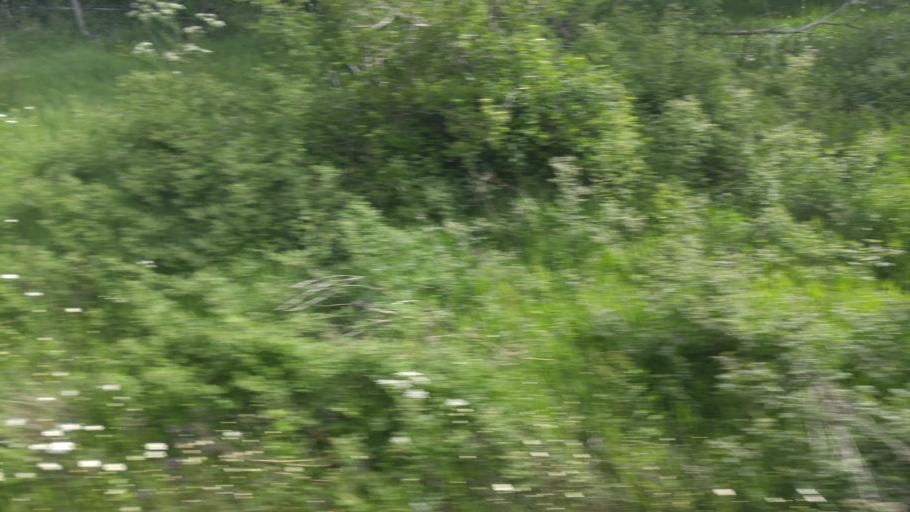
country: NO
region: Sor-Trondelag
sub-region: Melhus
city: Melhus
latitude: 63.2236
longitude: 10.2952
